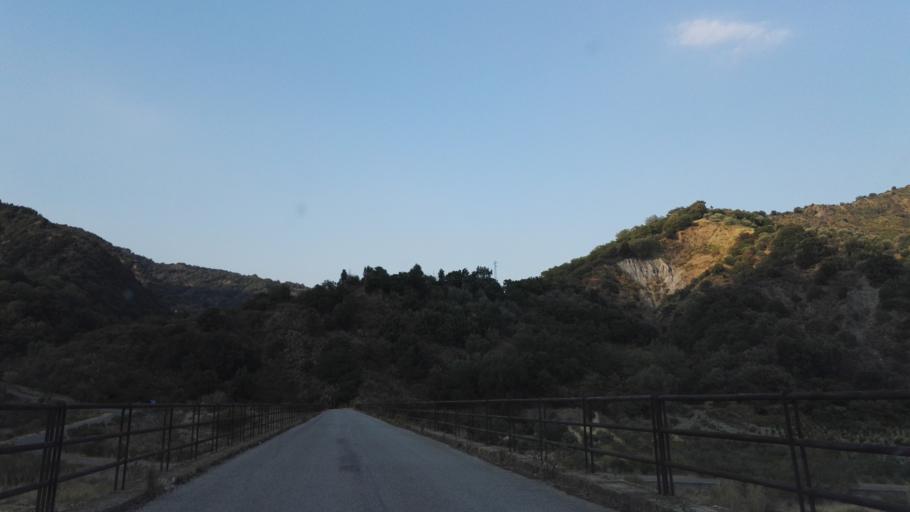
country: IT
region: Calabria
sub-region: Provincia di Reggio Calabria
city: Caulonia
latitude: 38.4184
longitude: 16.3776
